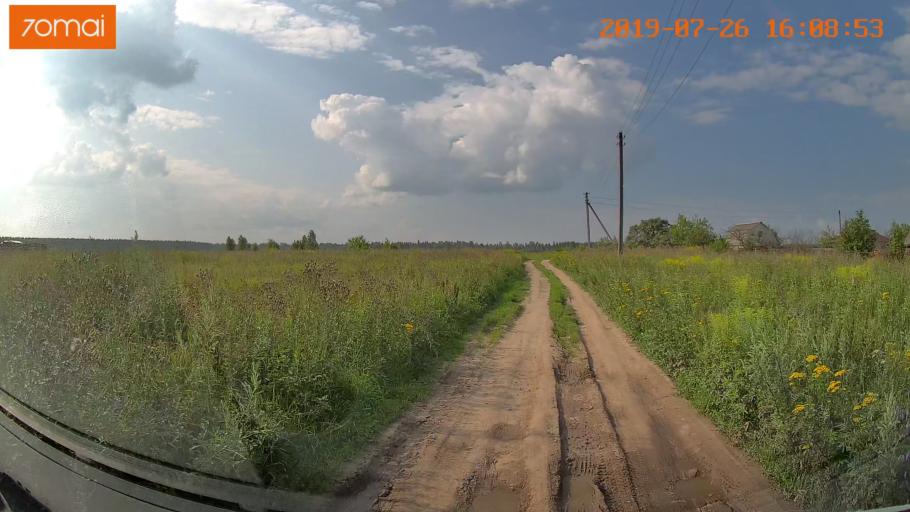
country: RU
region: Ivanovo
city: Bogorodskoye
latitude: 57.0628
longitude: 41.0581
